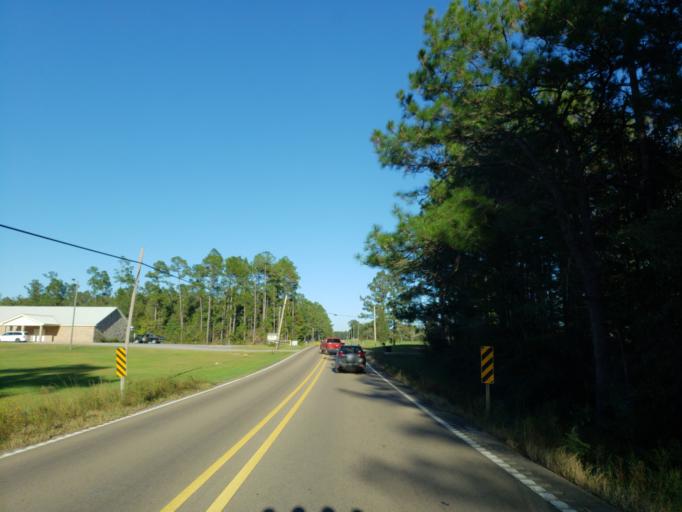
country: US
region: Mississippi
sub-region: Perry County
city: Richton
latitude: 31.3648
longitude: -88.8856
